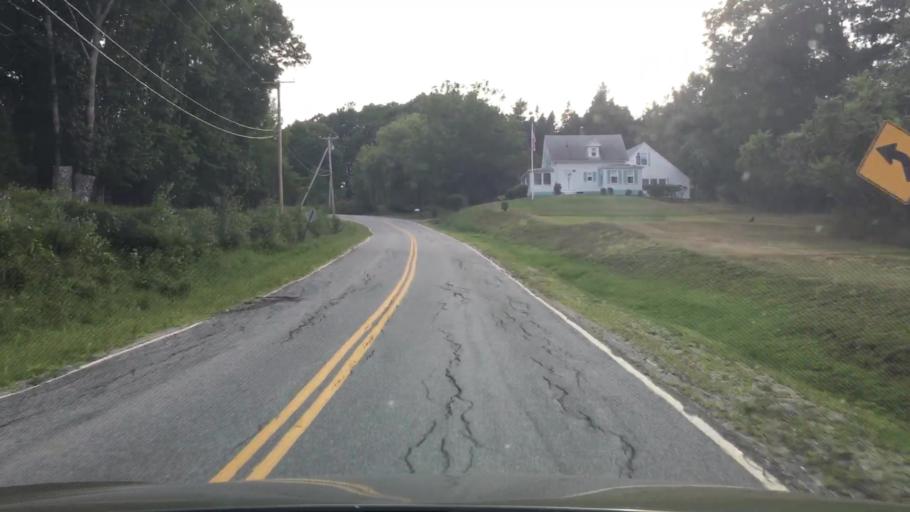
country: US
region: Maine
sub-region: Hancock County
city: Penobscot
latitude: 44.4739
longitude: -68.7271
